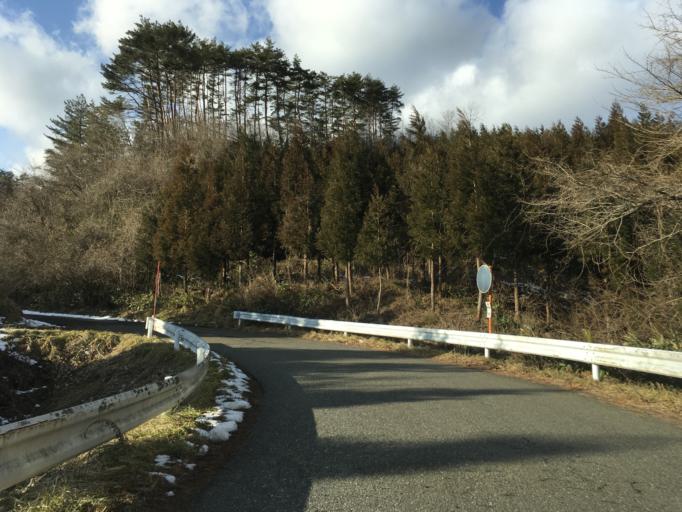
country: JP
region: Miyagi
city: Furukawa
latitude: 38.8181
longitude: 140.8326
